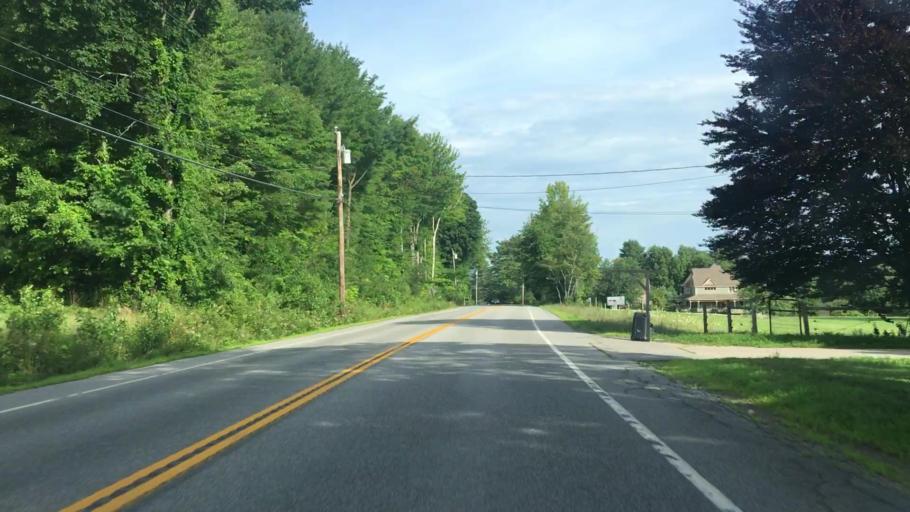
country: US
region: Maine
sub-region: York County
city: Cornish
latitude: 43.7834
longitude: -70.7591
